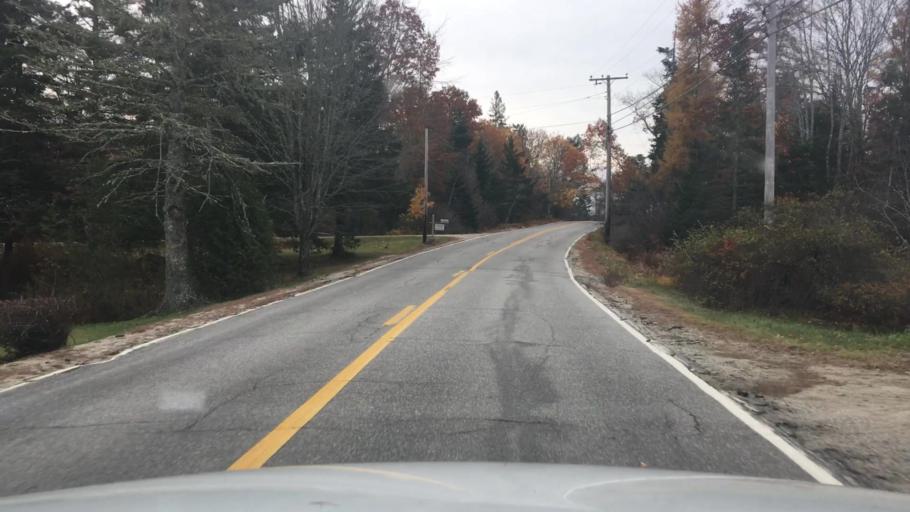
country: US
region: Maine
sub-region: Hancock County
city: Sedgwick
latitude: 44.3574
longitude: -68.5490
